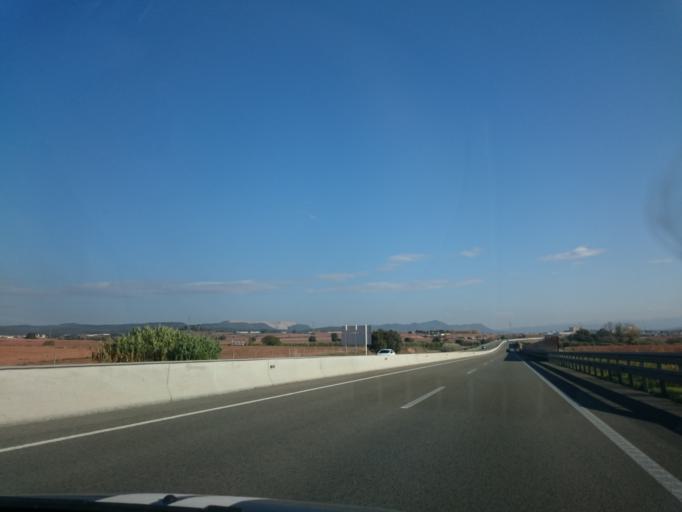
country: ES
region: Catalonia
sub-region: Provincia de Barcelona
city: Sant Fruitos de Bages
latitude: 41.7568
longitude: 1.8548
